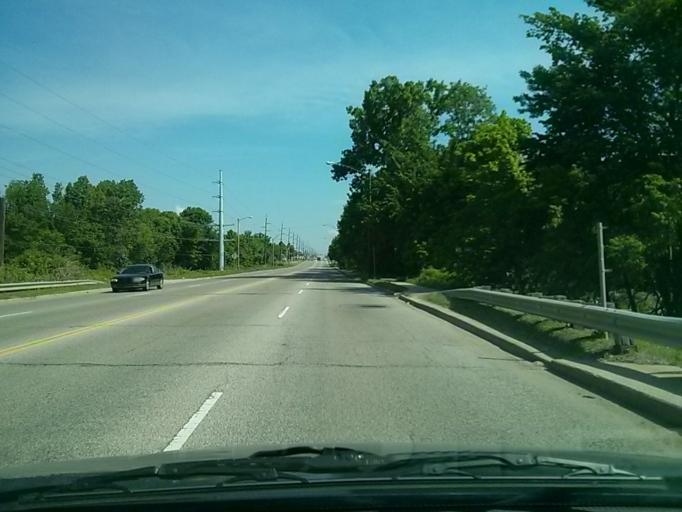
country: US
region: Oklahoma
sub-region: Tulsa County
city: Turley
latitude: 36.2133
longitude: -95.9755
